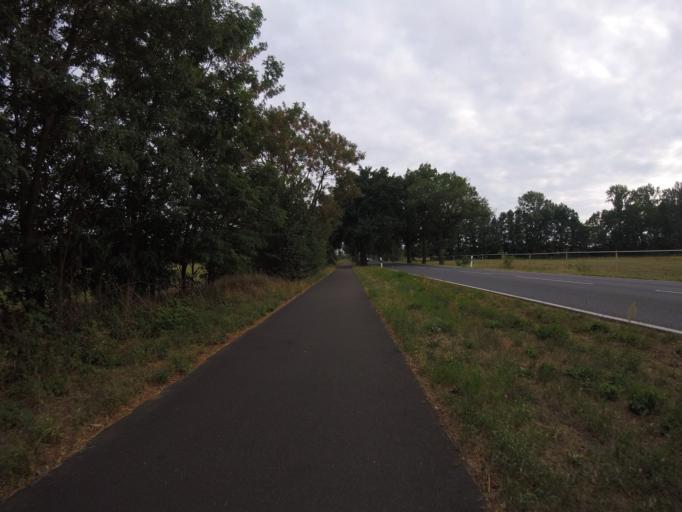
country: DE
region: Brandenburg
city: Liebenwalde
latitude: 52.8568
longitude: 13.3316
